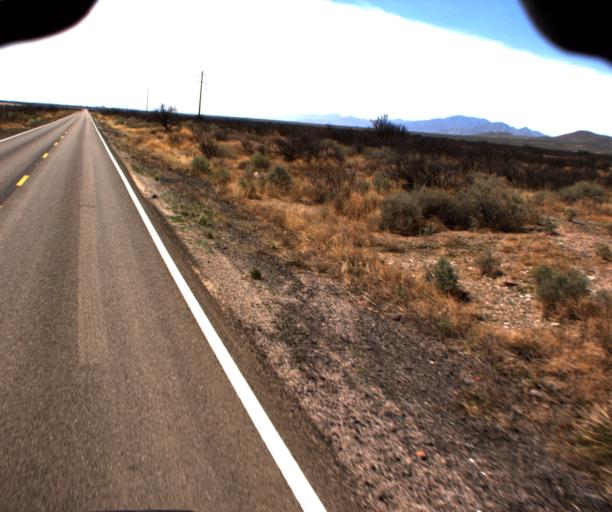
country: US
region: Arizona
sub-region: Cochise County
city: Willcox
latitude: 32.1639
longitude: -109.9431
